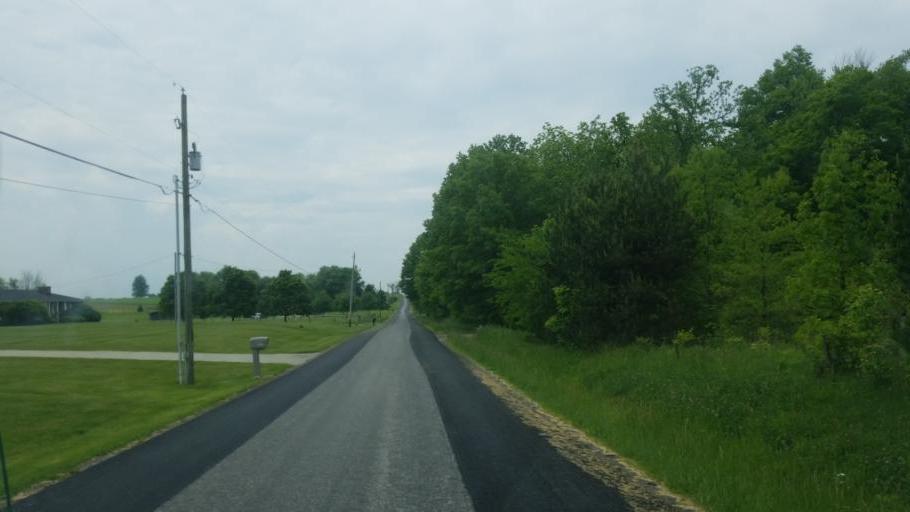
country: US
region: Ohio
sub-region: Wayne County
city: Orrville
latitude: 40.7827
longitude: -81.7578
